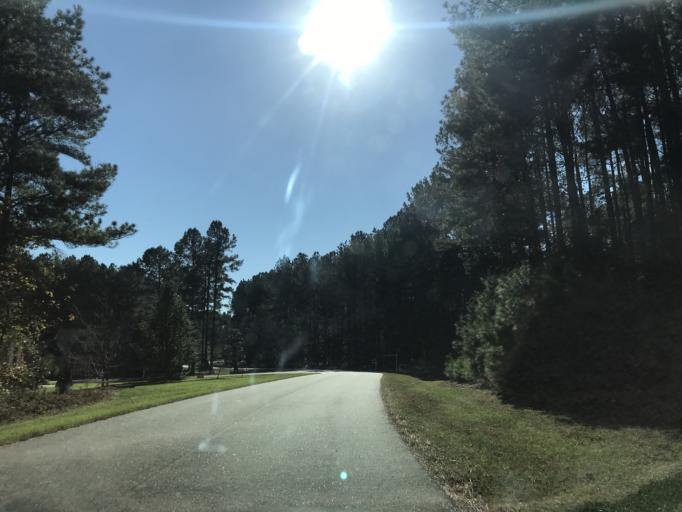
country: US
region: North Carolina
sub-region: Wake County
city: Rolesville
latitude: 35.9630
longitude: -78.3678
